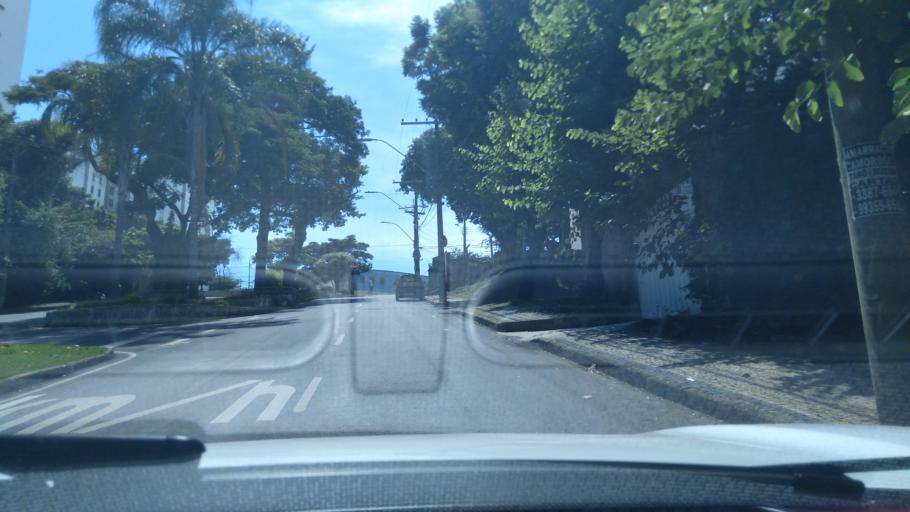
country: BR
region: Minas Gerais
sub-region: Contagem
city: Contagem
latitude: -19.9234
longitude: -44.0077
